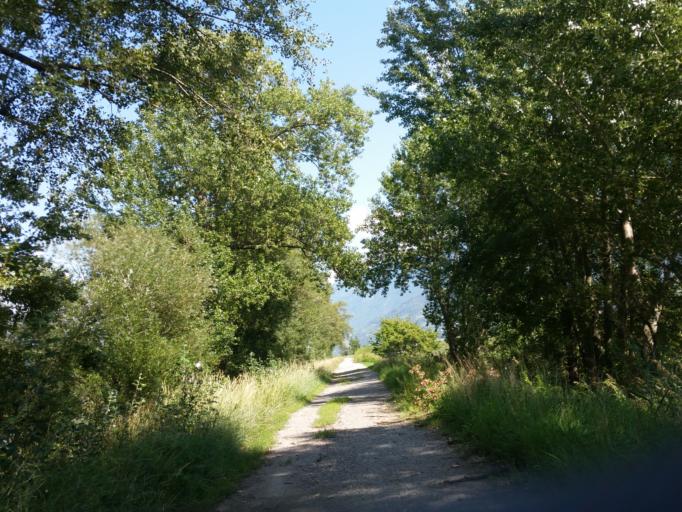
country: CH
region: Valais
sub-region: Martigny District
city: Fully
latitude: 46.1253
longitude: 7.0940
